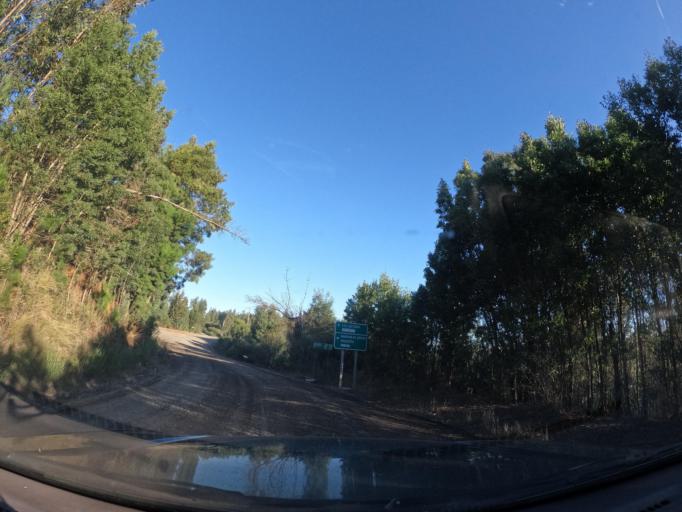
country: CL
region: Biobio
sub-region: Provincia de Concepcion
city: Chiguayante
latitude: -37.0293
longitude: -72.8718
